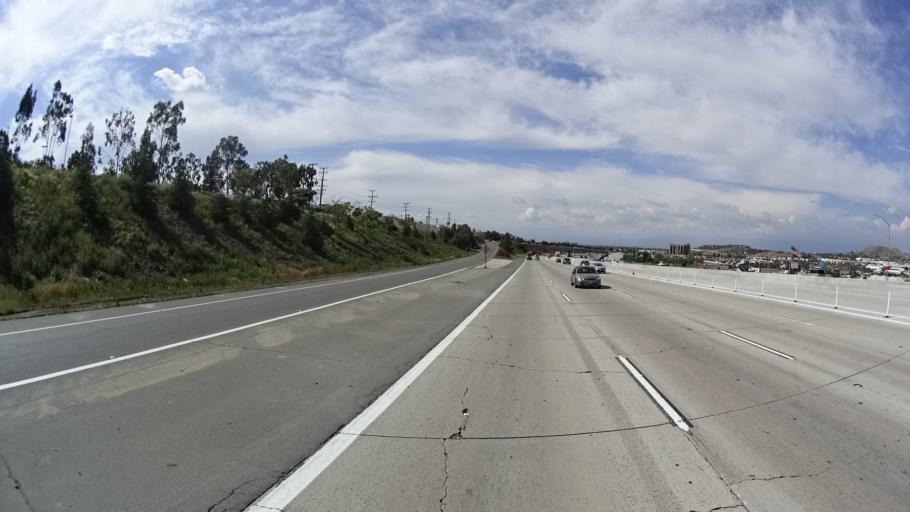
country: US
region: California
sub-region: Riverside County
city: Home Gardens
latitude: 33.8633
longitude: -117.5399
